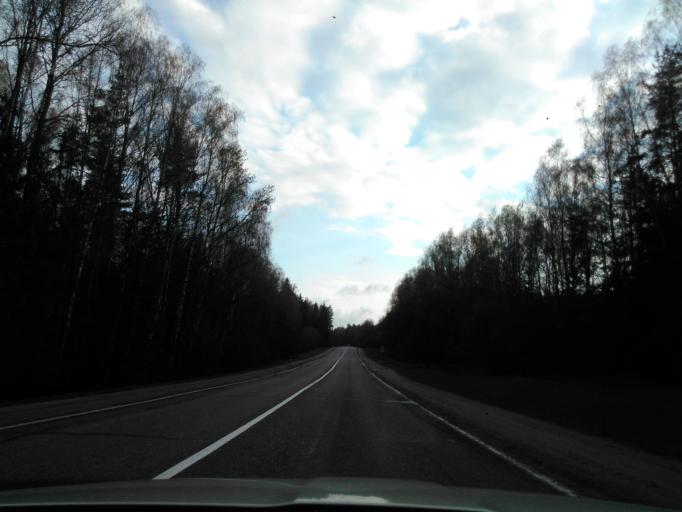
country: BY
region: Minsk
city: Lahoysk
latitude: 54.2851
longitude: 27.8676
